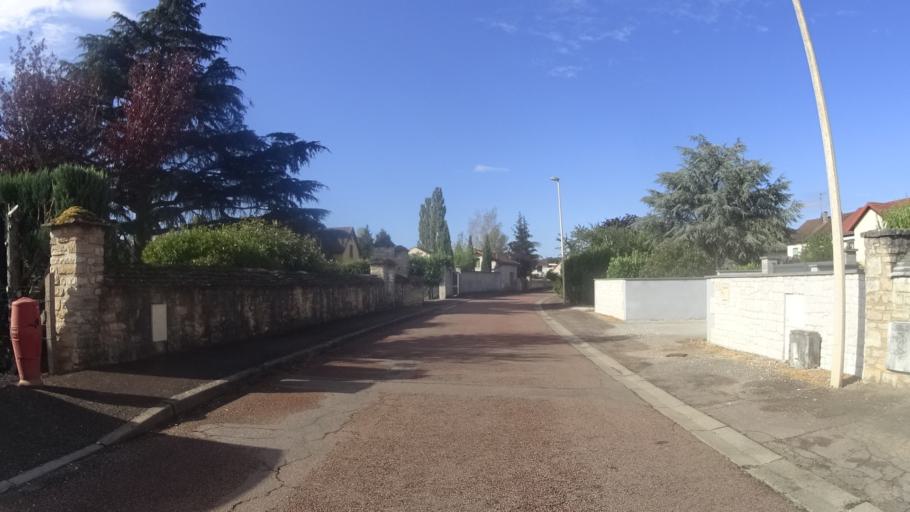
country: FR
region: Bourgogne
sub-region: Departement de Saone-et-Loire
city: Chagny
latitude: 46.9191
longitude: 4.7559
